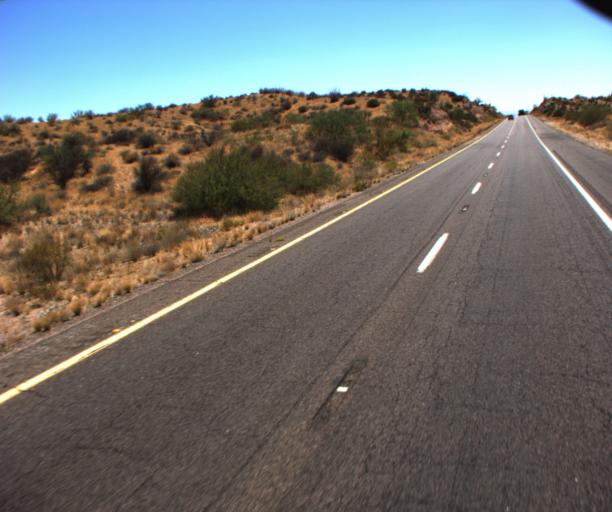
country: US
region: Arizona
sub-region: Maricopa County
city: Rio Verde
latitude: 33.6421
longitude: -111.5408
